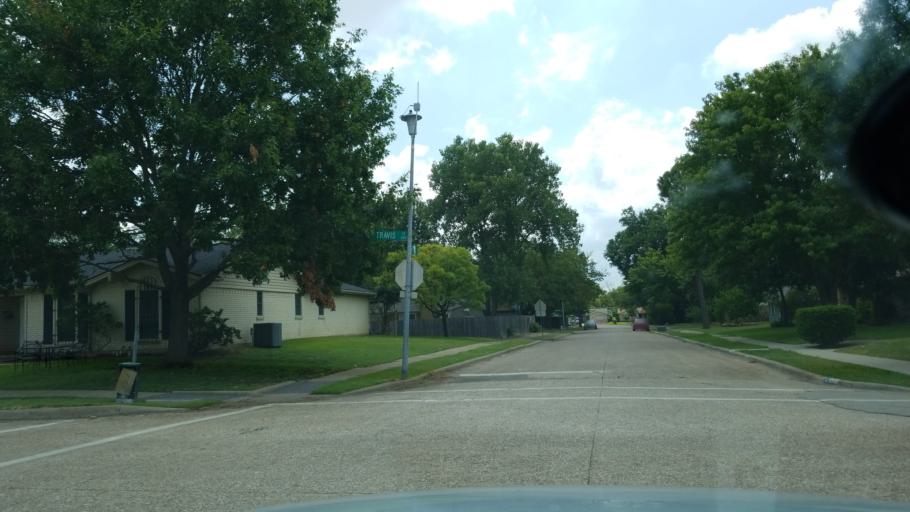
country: US
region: Texas
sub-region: Dallas County
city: Garland
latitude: 32.9244
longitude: -96.6529
